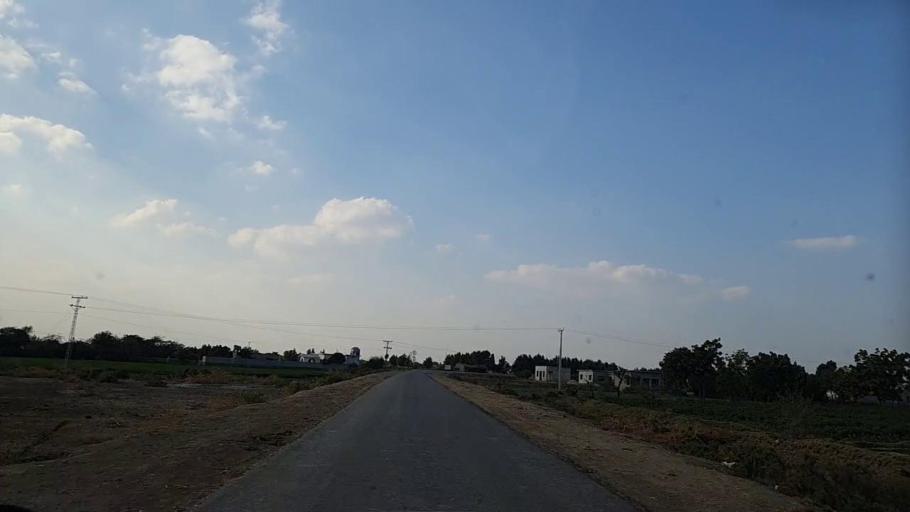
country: PK
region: Sindh
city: Pithoro
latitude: 25.6860
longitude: 69.2238
